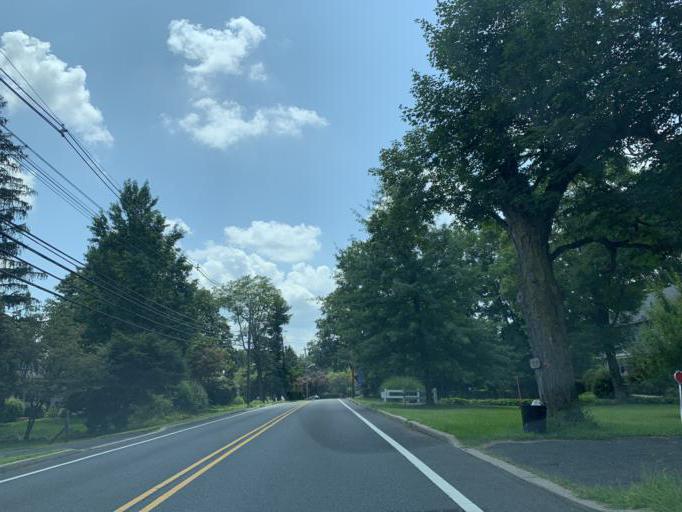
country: US
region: New Jersey
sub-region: Somerset County
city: Bernardsville
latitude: 40.7077
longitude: -74.5675
